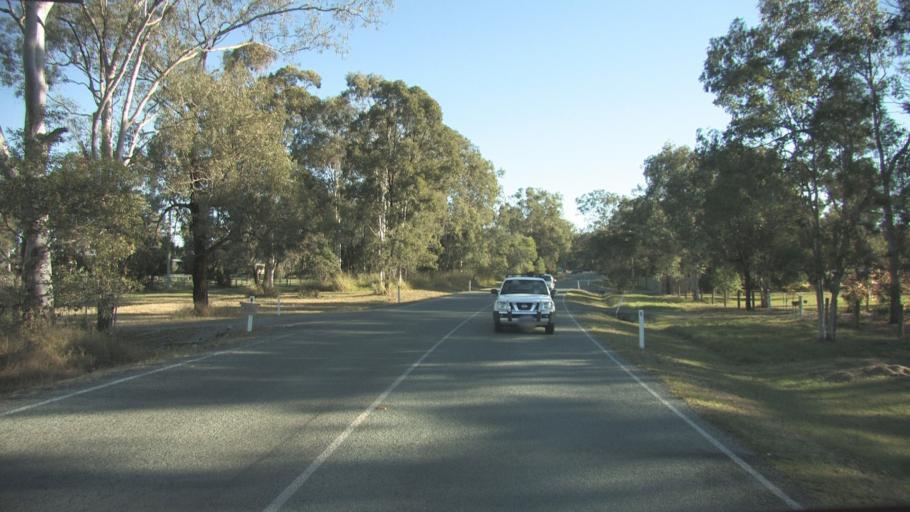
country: AU
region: Queensland
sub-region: Logan
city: Chambers Flat
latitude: -27.7489
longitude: 153.0579
